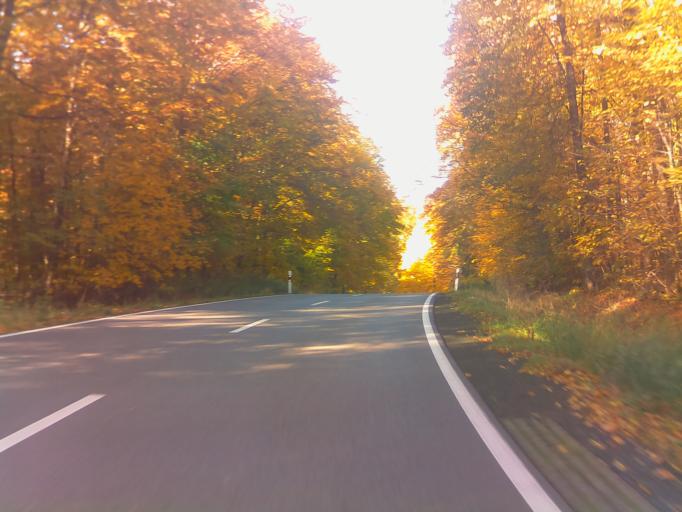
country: DE
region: Bavaria
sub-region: Regierungsbezirk Unterfranken
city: Knetzgau
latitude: 49.9274
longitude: 10.5655
